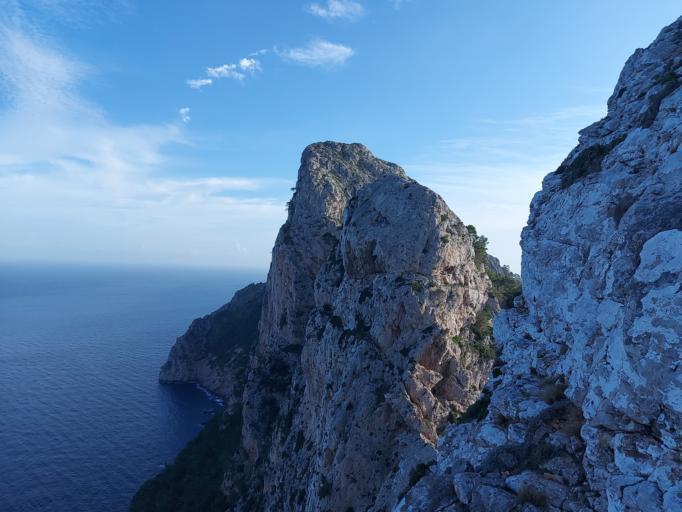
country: ES
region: Balearic Islands
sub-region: Illes Balears
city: Alcudia
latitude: 39.9443
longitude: 3.1378
